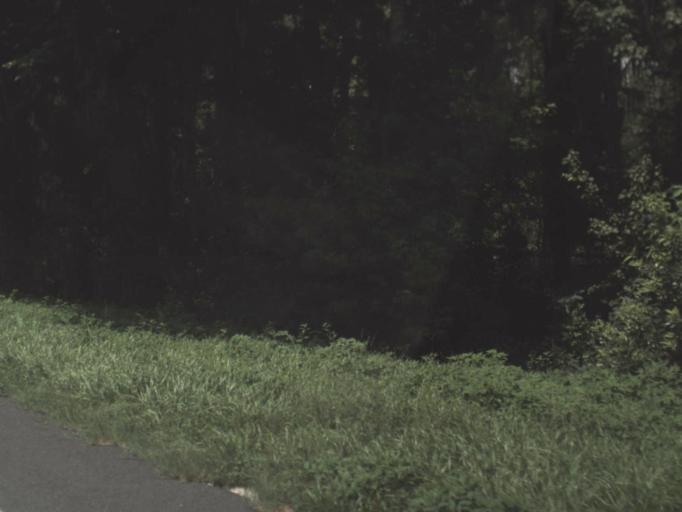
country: US
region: Florida
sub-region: Suwannee County
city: Wellborn
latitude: 30.3818
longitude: -82.8144
